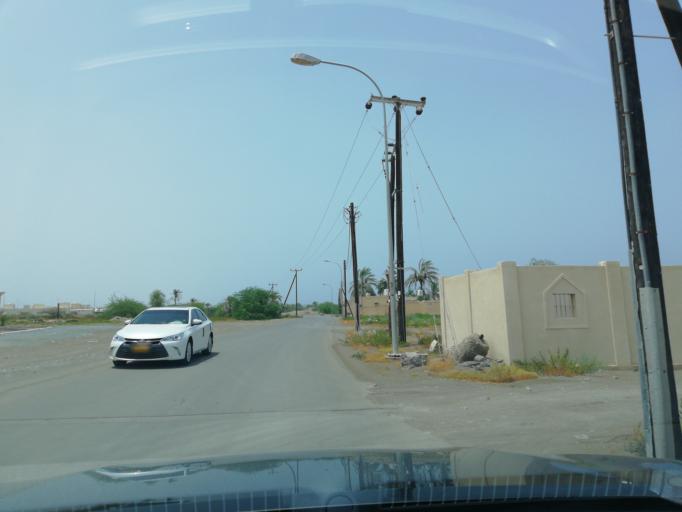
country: OM
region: Al Batinah
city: Al Liwa'
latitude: 24.6113
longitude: 56.5375
